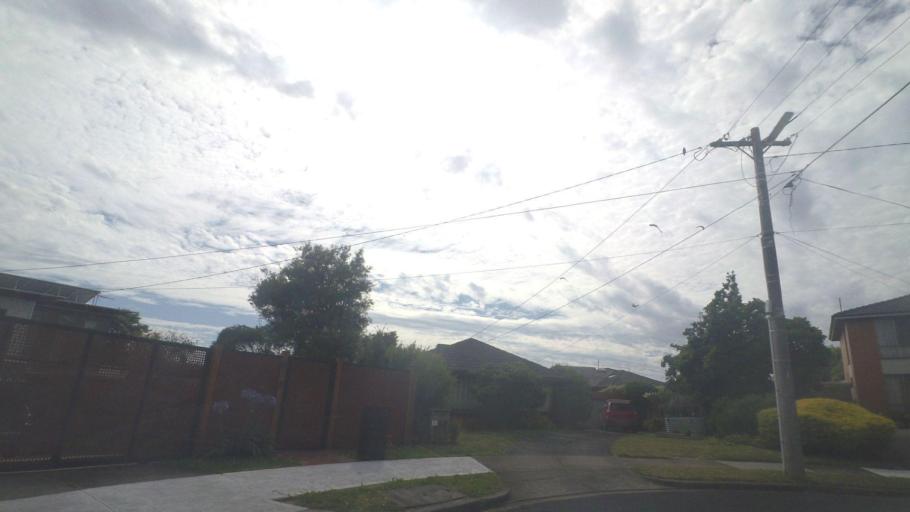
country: AU
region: Victoria
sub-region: Banyule
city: Viewbank
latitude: -37.7456
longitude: 145.0829
